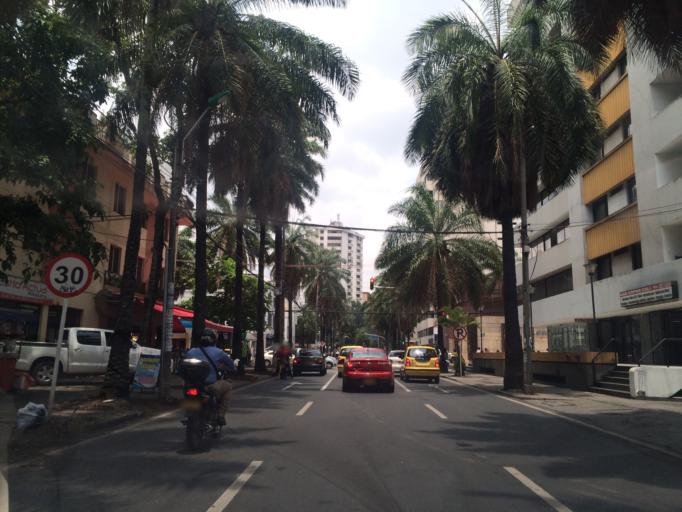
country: CO
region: Valle del Cauca
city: Cali
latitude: 3.4621
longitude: -76.5291
